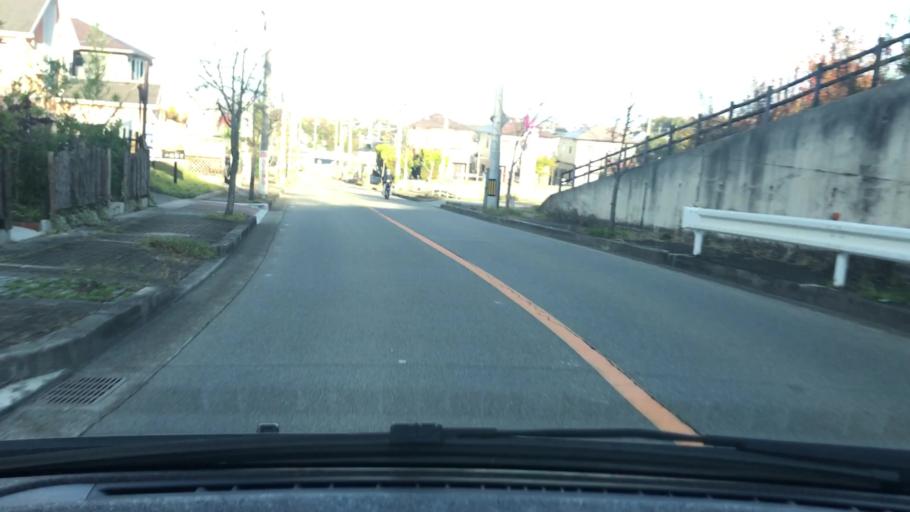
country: JP
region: Hyogo
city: Sandacho
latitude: 34.8253
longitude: 135.2518
